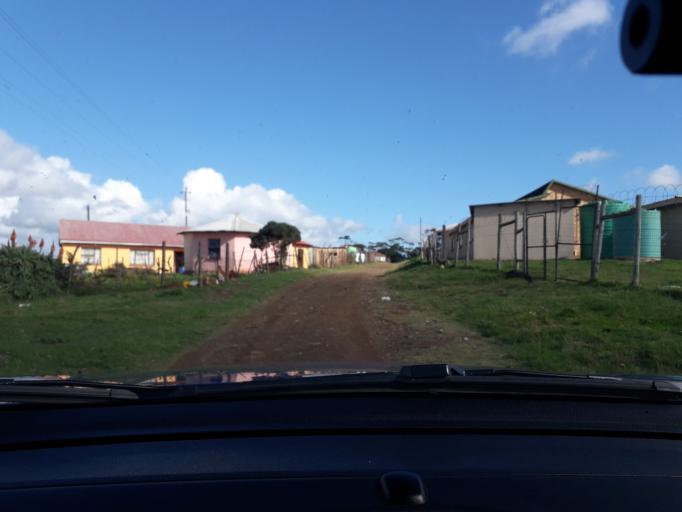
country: ZA
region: Eastern Cape
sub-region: Buffalo City Metropolitan Municipality
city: Bhisho
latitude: -33.1106
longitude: 27.4270
